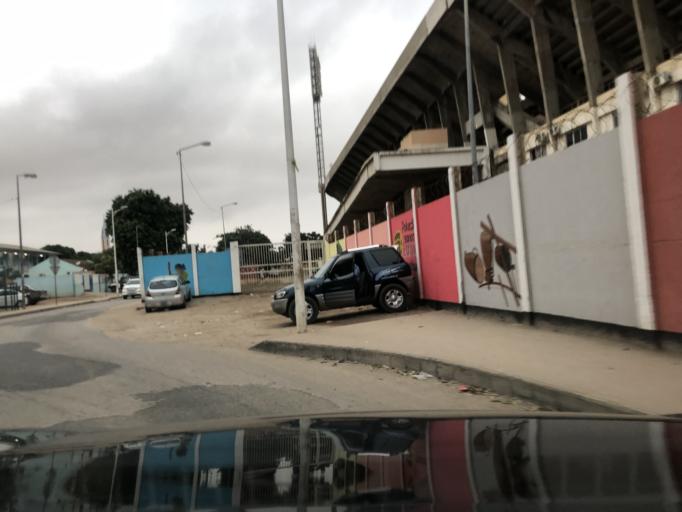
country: AO
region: Luanda
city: Luanda
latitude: -8.8271
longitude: 13.2570
